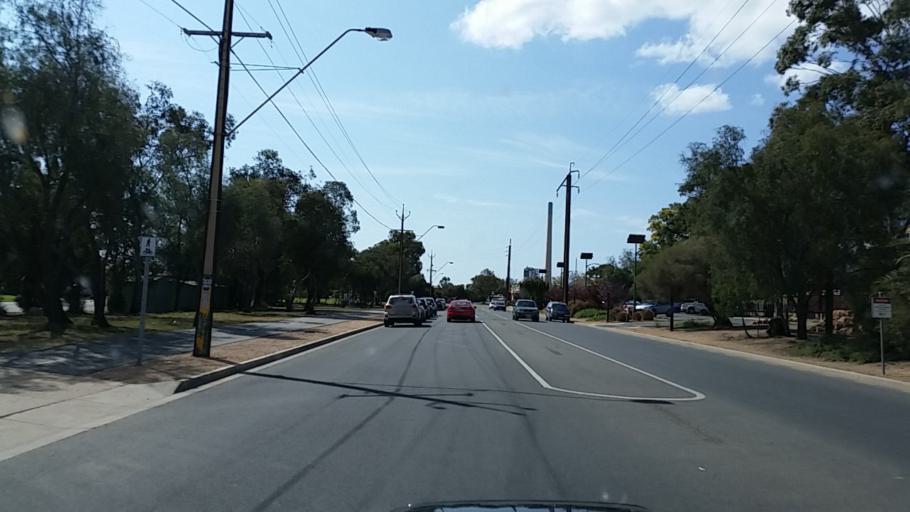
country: AU
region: South Australia
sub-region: Port Pirie City and Dists
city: Port Pirie
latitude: -33.1835
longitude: 138.0113
